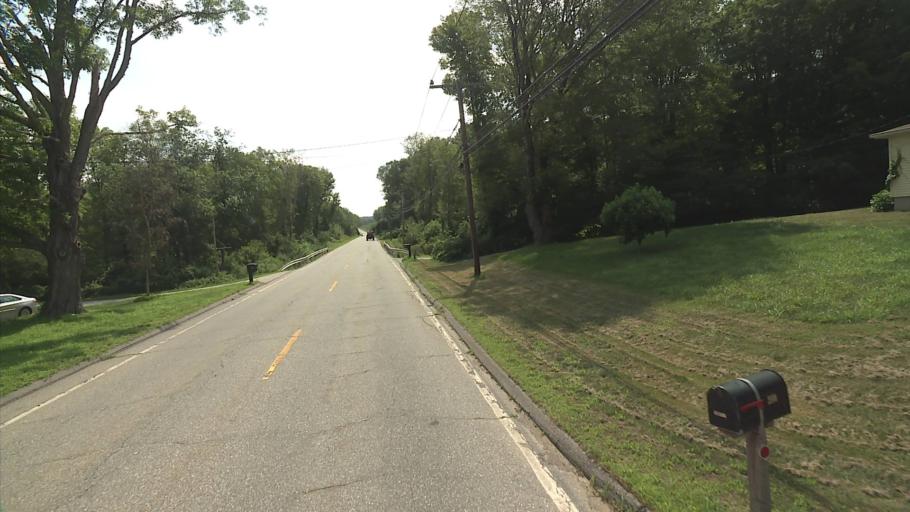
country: US
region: Connecticut
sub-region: New London County
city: Preston City
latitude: 41.5314
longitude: -71.9982
